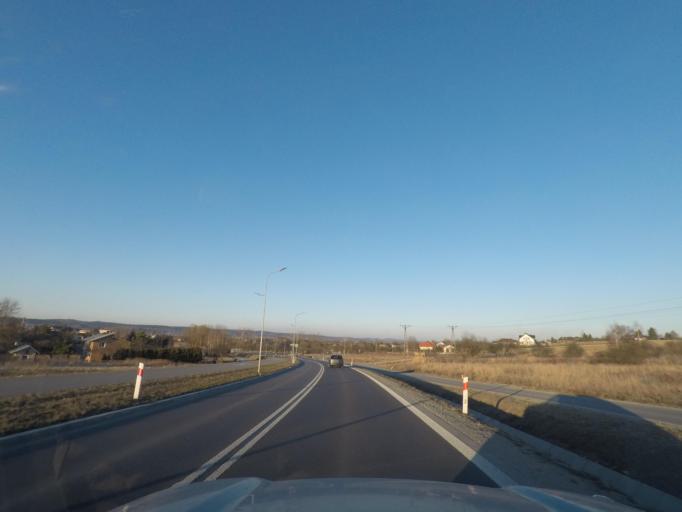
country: PL
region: Subcarpathian Voivodeship
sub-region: Powiat jasielski
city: Jaslo
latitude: 49.7310
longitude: 21.4822
